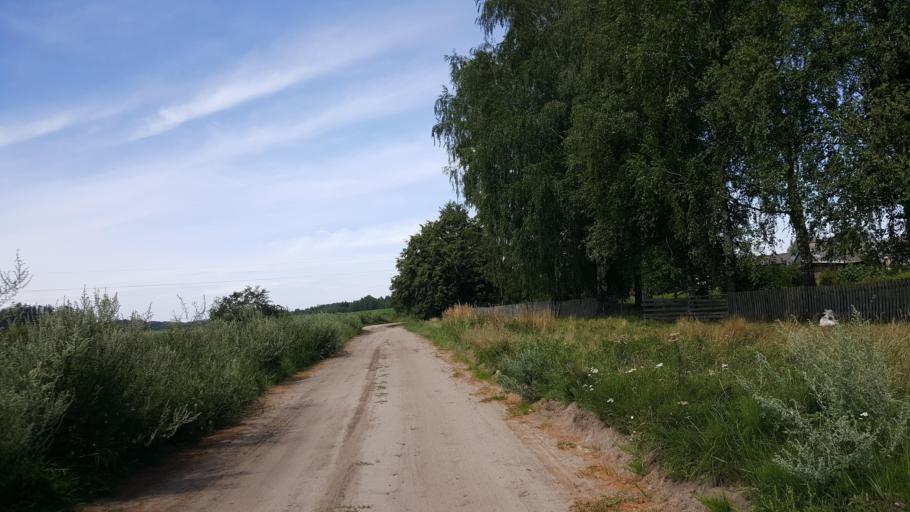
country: BY
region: Brest
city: Pruzhany
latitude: 52.5618
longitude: 24.2050
